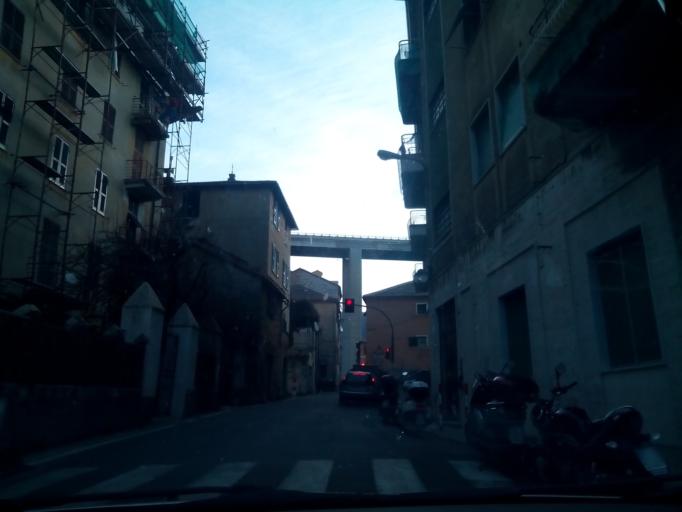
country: IT
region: Liguria
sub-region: Provincia di Genova
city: Genoa
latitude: 44.4101
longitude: 8.9882
